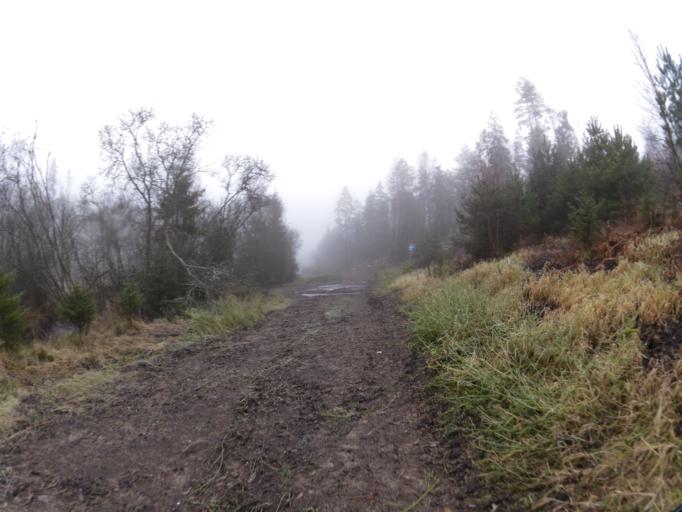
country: NO
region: Ostfold
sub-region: Fredrikstad
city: Fredrikstad
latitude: 59.2599
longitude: 10.9753
